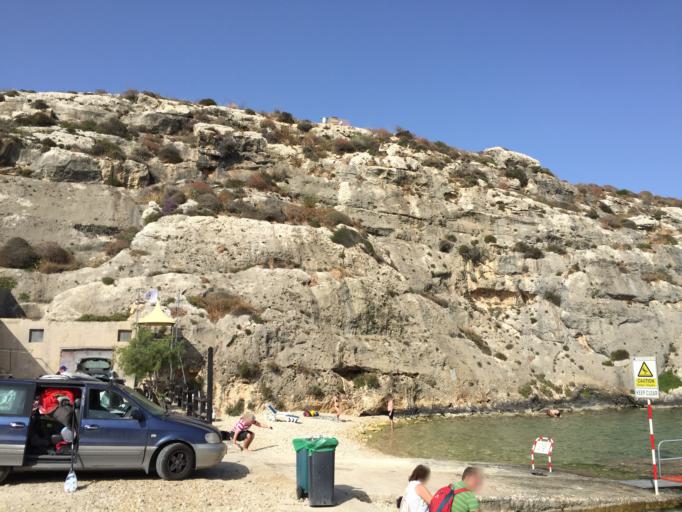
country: MT
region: Ghajnsielem
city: Ghajnsielem
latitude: 36.0204
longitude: 14.2711
